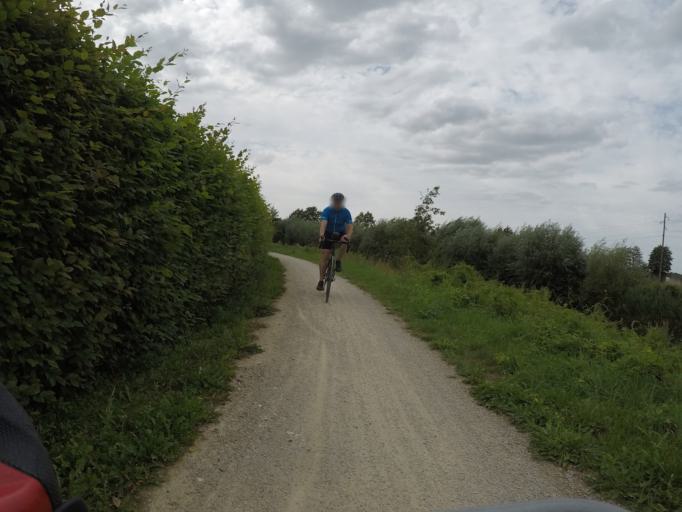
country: DE
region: Lower Saxony
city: Bardowick
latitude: 53.2976
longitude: 10.4006
